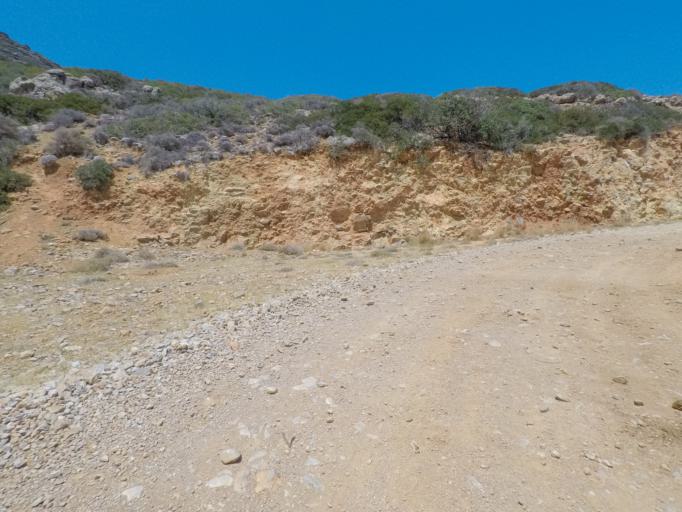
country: GR
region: Crete
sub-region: Nomos Lasithiou
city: Elounda
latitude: 35.3222
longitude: 25.7578
